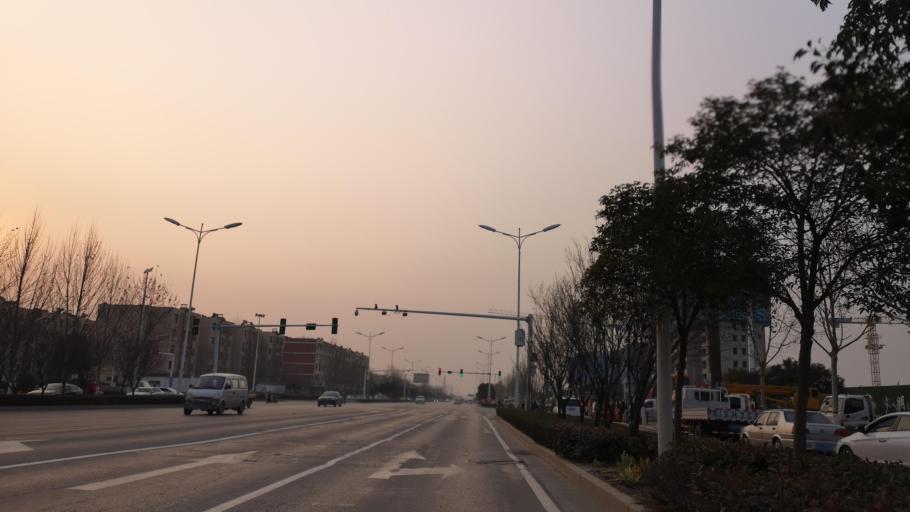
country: CN
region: Henan Sheng
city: Zhongyuanlu
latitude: 35.7893
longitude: 115.0832
